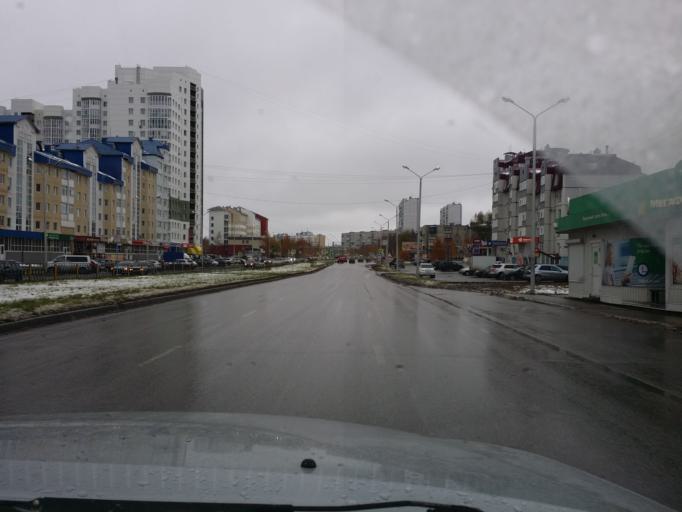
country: RU
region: Khanty-Mansiyskiy Avtonomnyy Okrug
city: Nizhnevartovsk
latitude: 60.9372
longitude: 76.5808
